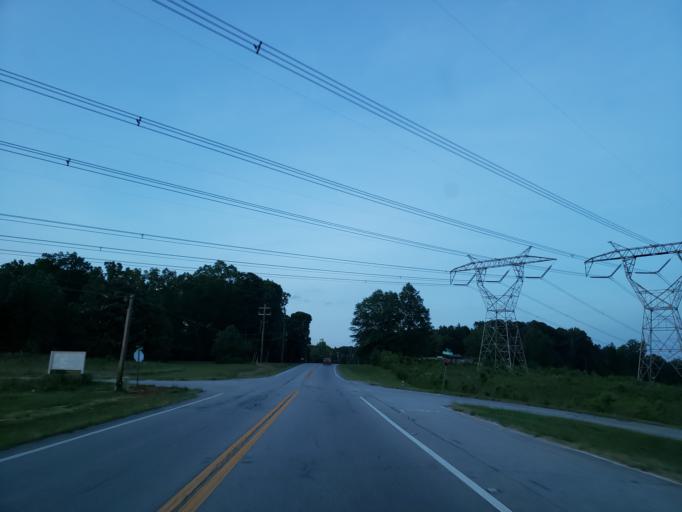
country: US
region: Georgia
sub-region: Douglas County
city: Douglasville
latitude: 33.6999
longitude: -84.7851
